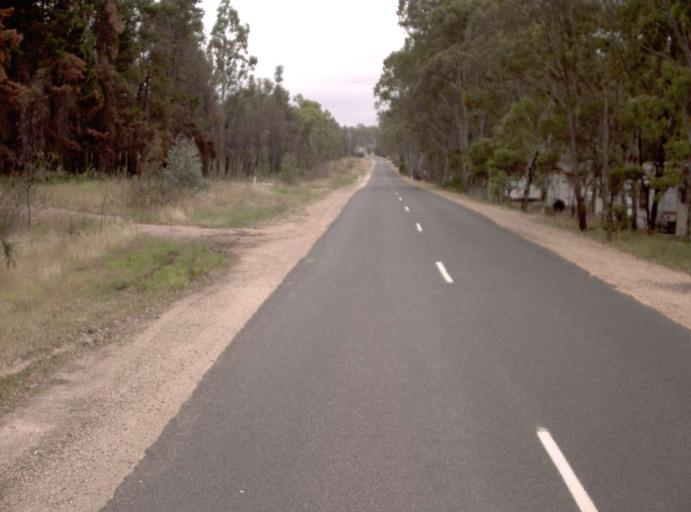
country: AU
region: Victoria
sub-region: Wellington
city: Heyfield
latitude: -37.9135
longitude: 146.7554
